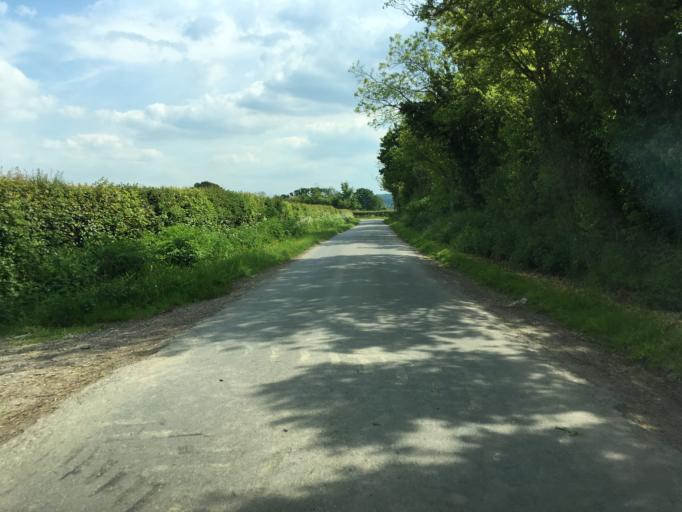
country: GB
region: England
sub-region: South Gloucestershire
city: Thornbury
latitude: 51.6258
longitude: -2.5538
